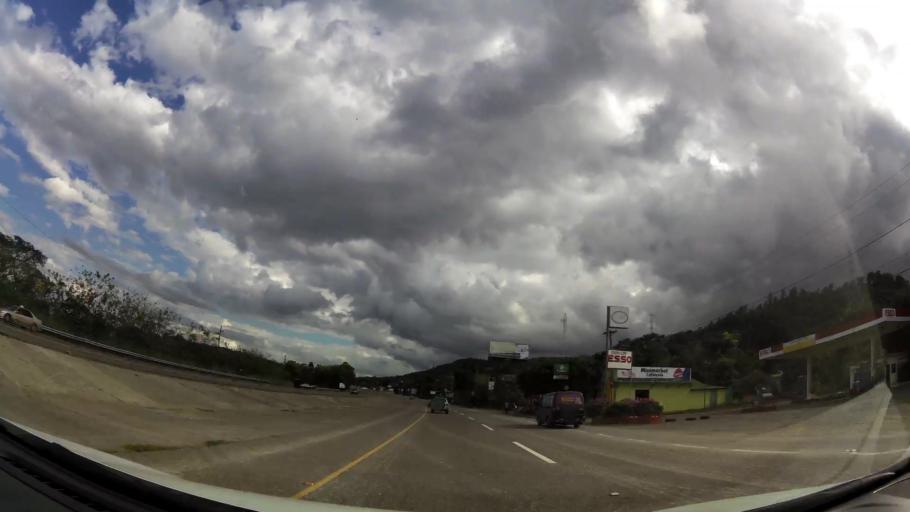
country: DO
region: La Vega
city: Concepcion de La Vega
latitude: 19.1566
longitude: -70.4831
